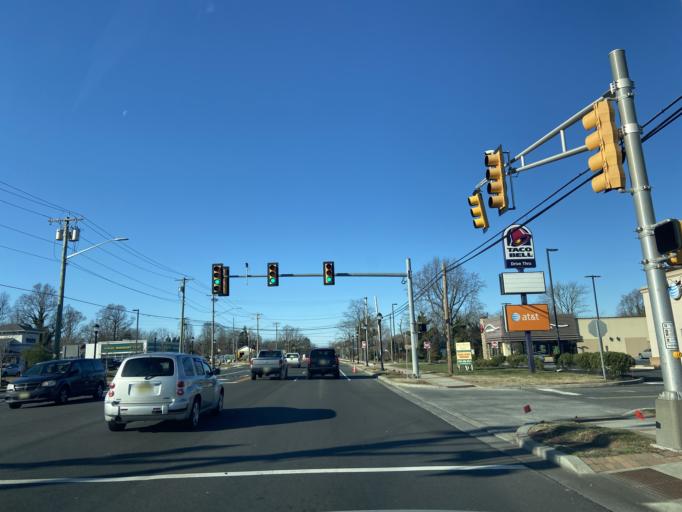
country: US
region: New Jersey
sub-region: Cumberland County
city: Vineland
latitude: 39.4876
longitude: -75.0489
